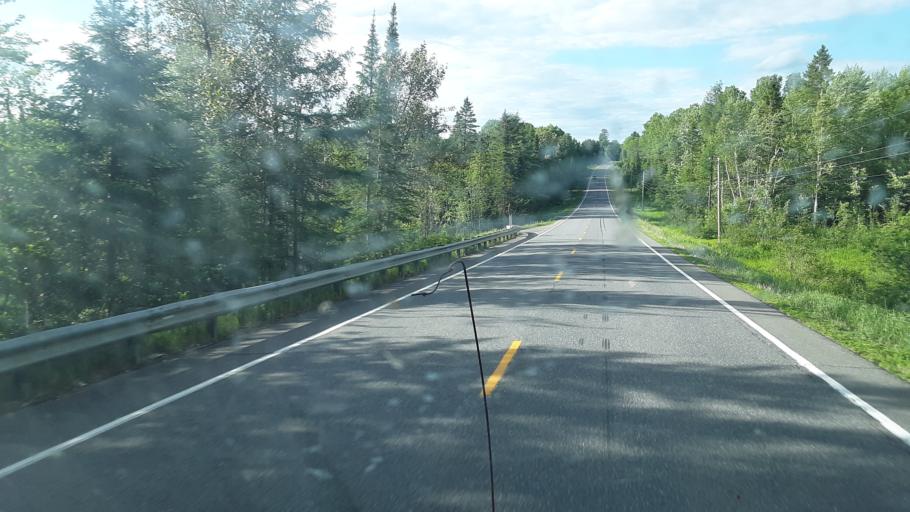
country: US
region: Maine
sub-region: Aroostook County
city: Presque Isle
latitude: 46.4709
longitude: -68.3888
